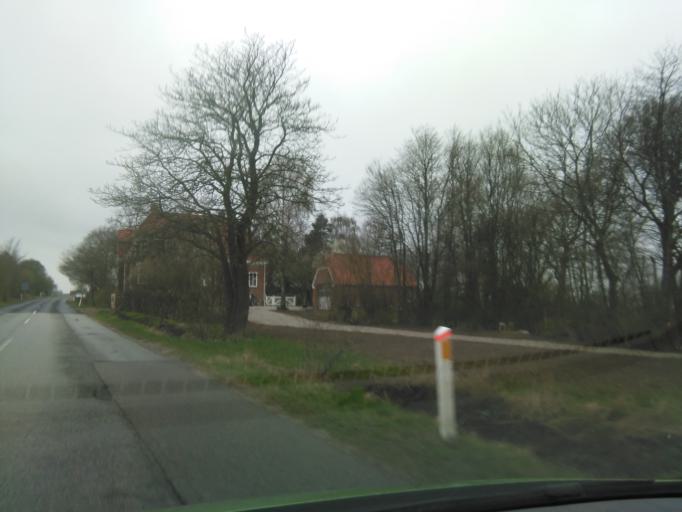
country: DK
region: Central Jutland
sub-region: Arhus Kommune
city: Kolt
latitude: 56.1289
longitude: 10.0794
